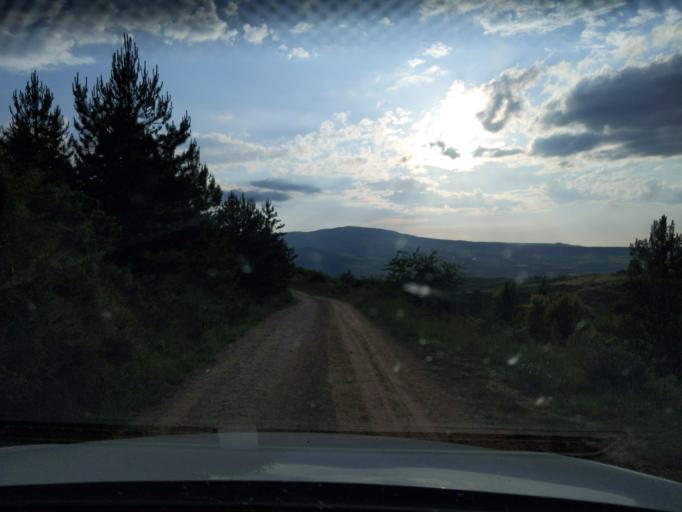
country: ES
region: La Rioja
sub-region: Provincia de La Rioja
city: Nalda
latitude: 42.3253
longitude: -2.4719
